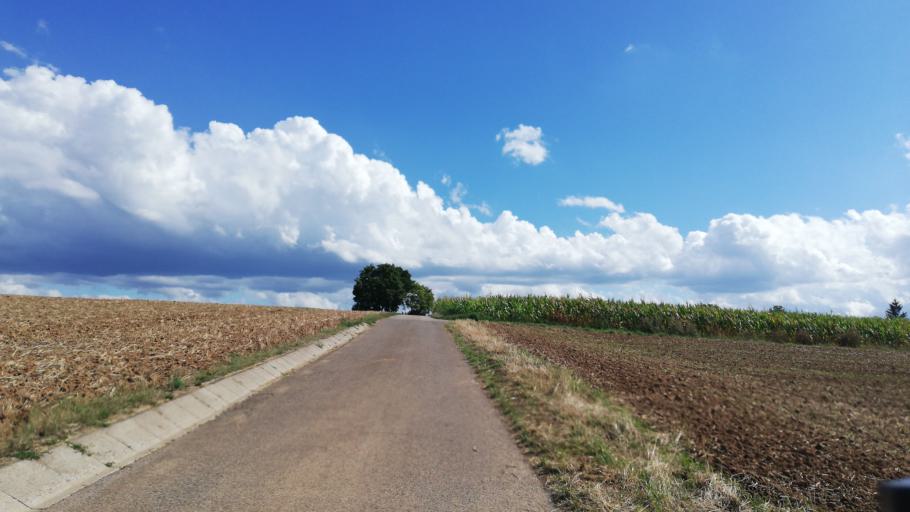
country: DE
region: Baden-Wuerttemberg
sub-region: Regierungsbezirk Stuttgart
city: Waiblingen
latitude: 48.8716
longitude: 9.2877
